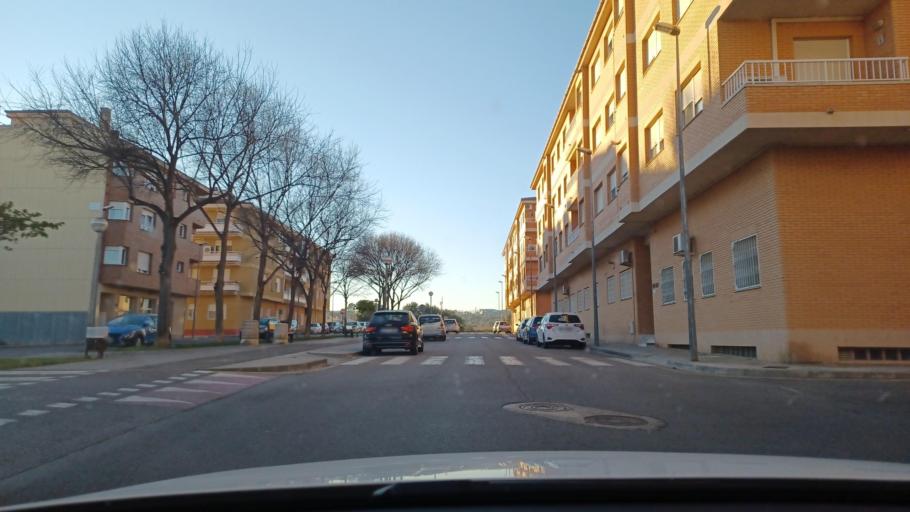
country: ES
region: Catalonia
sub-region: Provincia de Tarragona
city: Amposta
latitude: 40.7041
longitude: 0.5736
